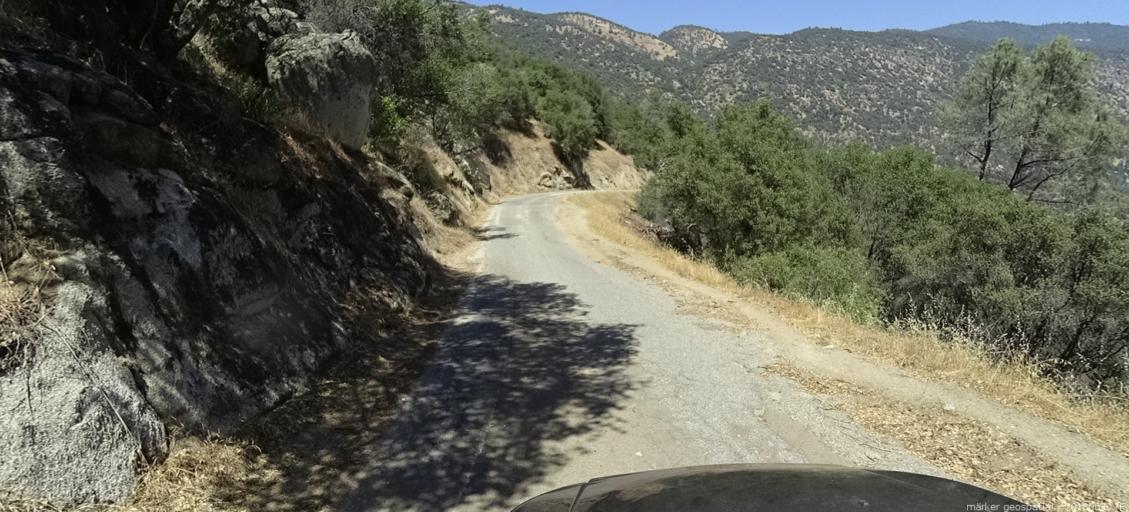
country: US
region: California
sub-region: Fresno County
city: Auberry
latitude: 37.1613
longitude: -119.4439
